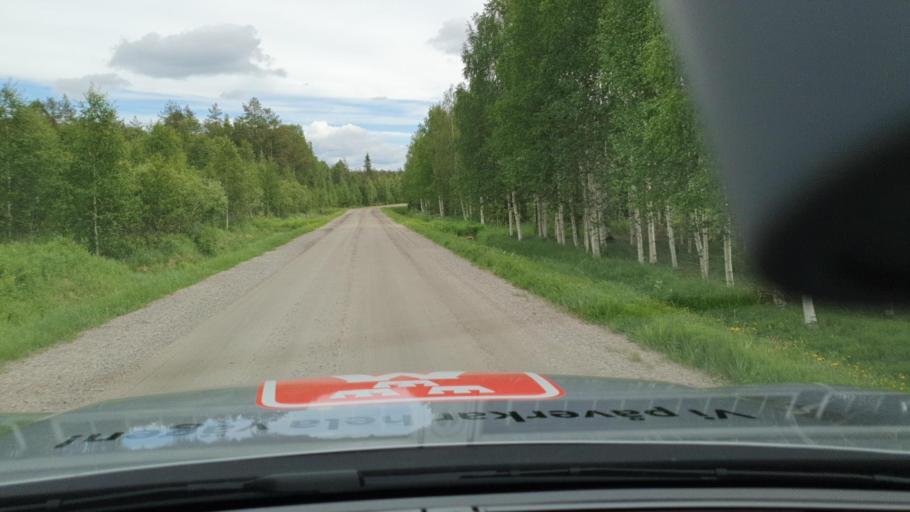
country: SE
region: Norrbotten
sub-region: Kalix Kommun
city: Kalix
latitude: 65.9399
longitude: 23.5303
